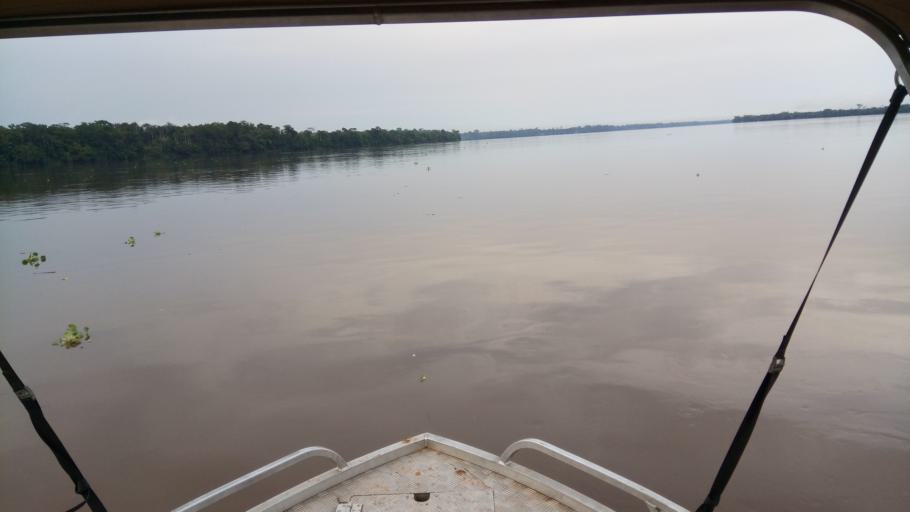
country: CD
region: Eastern Province
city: Kisangani
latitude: 0.5744
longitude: 24.8031
